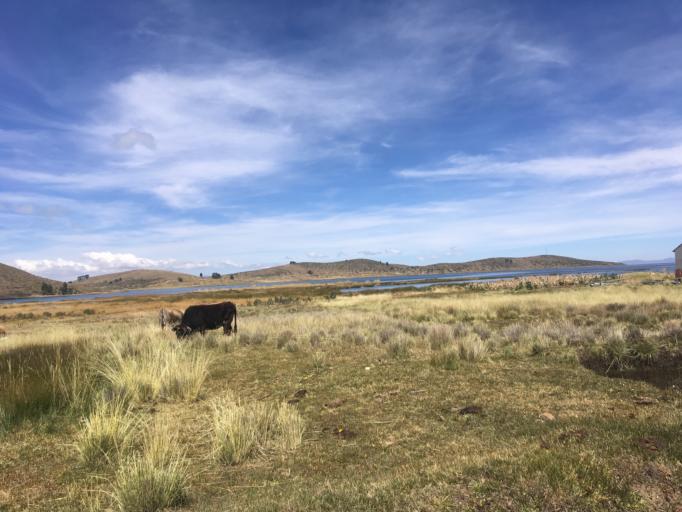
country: BO
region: La Paz
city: San Pedro
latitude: -16.2626
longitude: -68.8749
